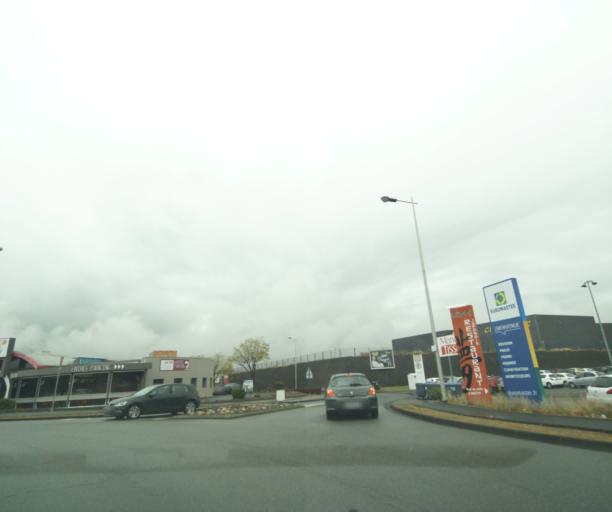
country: FR
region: Auvergne
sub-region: Departement du Puy-de-Dome
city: Perignat-les-Sarlieve
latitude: 45.7555
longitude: 3.1455
